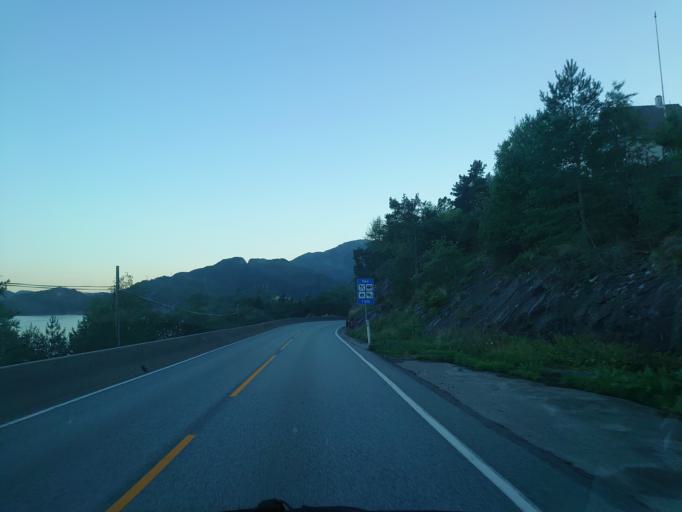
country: NO
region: Hordaland
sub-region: Osteroy
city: Lonevag
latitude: 60.7045
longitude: 5.6063
